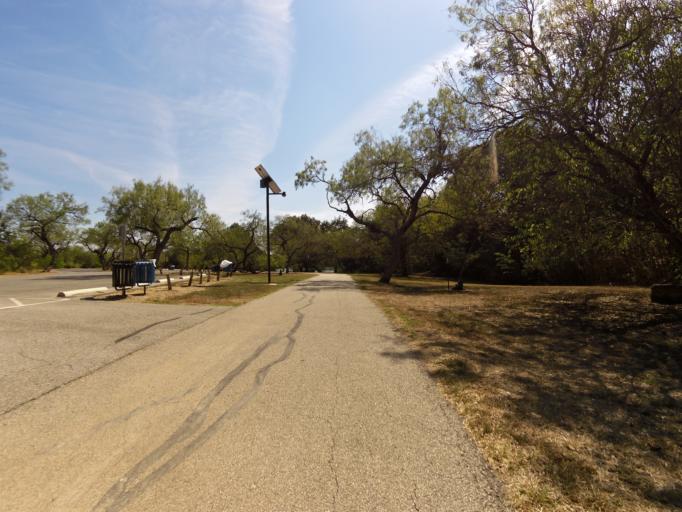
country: US
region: Texas
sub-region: Bexar County
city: San Antonio
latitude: 29.3880
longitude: -98.4289
